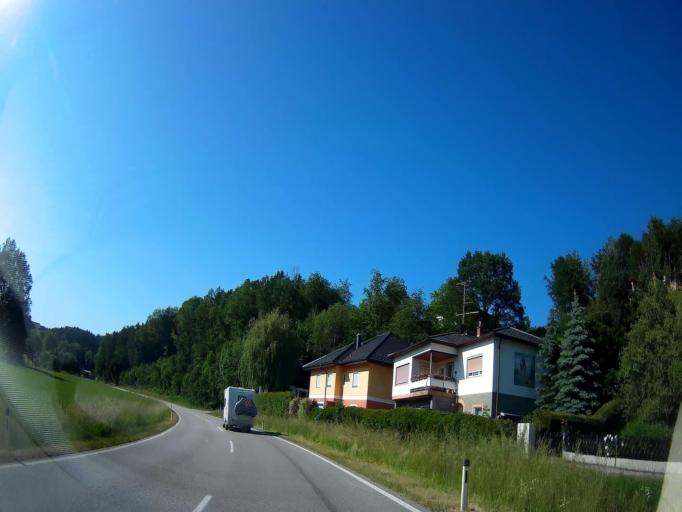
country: DE
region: Bavaria
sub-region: Lower Bavaria
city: Kirchdorf am Inn
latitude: 48.1384
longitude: 13.0189
